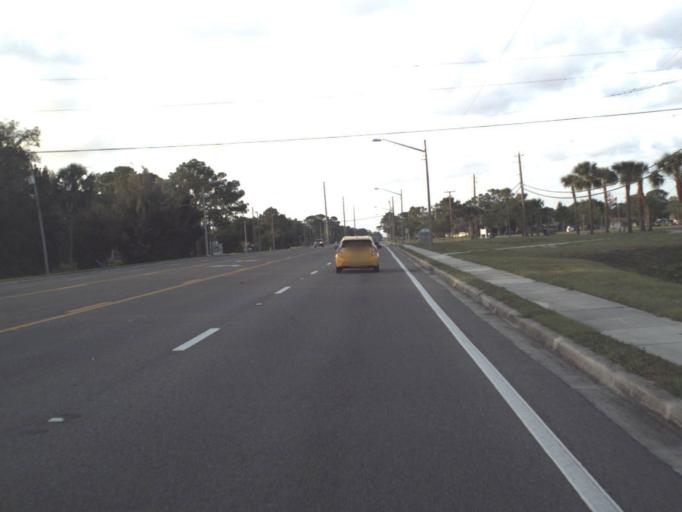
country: US
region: Florida
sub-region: Brevard County
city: Rockledge
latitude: 28.3132
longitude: -80.7427
